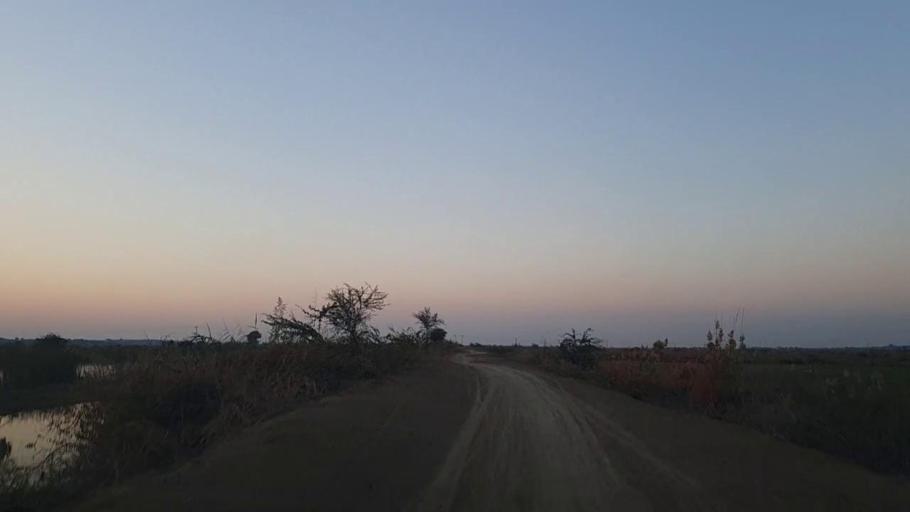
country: PK
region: Sindh
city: Tando Mittha Khan
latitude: 26.0656
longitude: 69.1612
